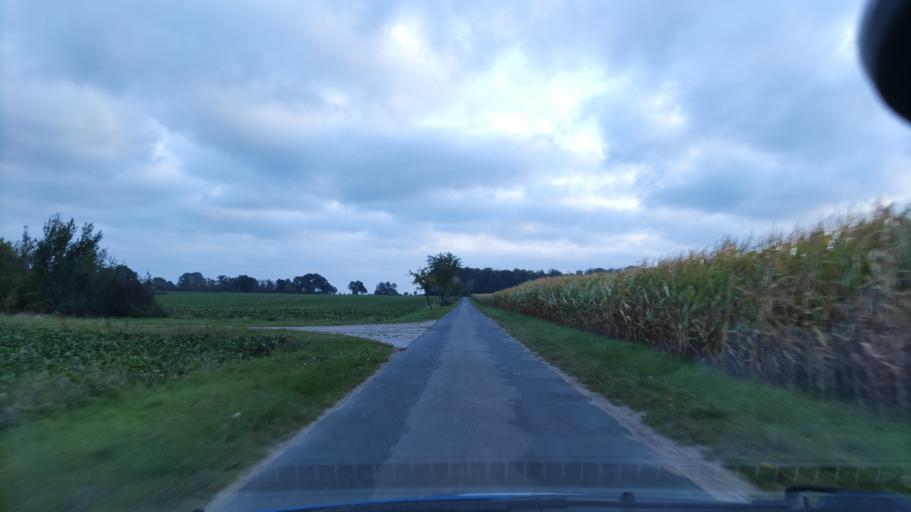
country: DE
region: Lower Saxony
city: Tosterglope
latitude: 53.2287
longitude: 10.8289
